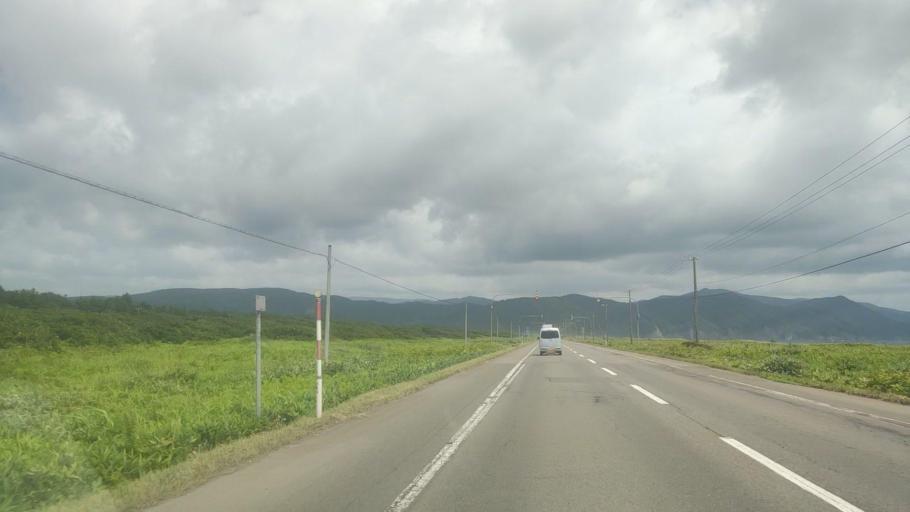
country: JP
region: Hokkaido
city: Niseko Town
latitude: 42.5664
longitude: 140.4384
